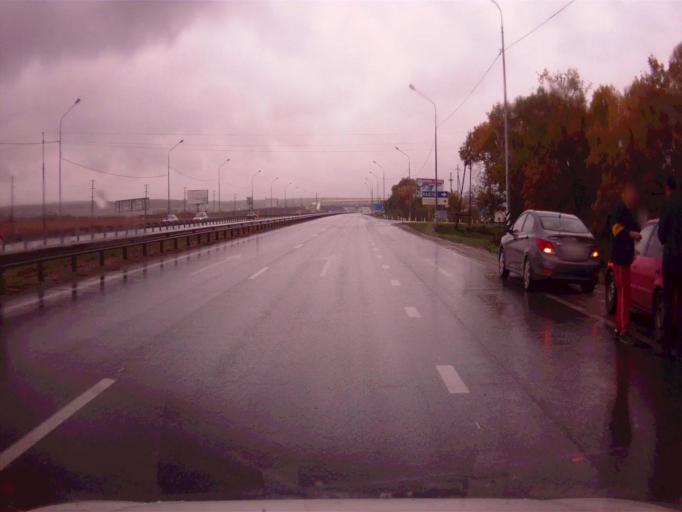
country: RU
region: Chelyabinsk
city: Dolgoderevenskoye
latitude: 55.3075
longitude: 61.3355
